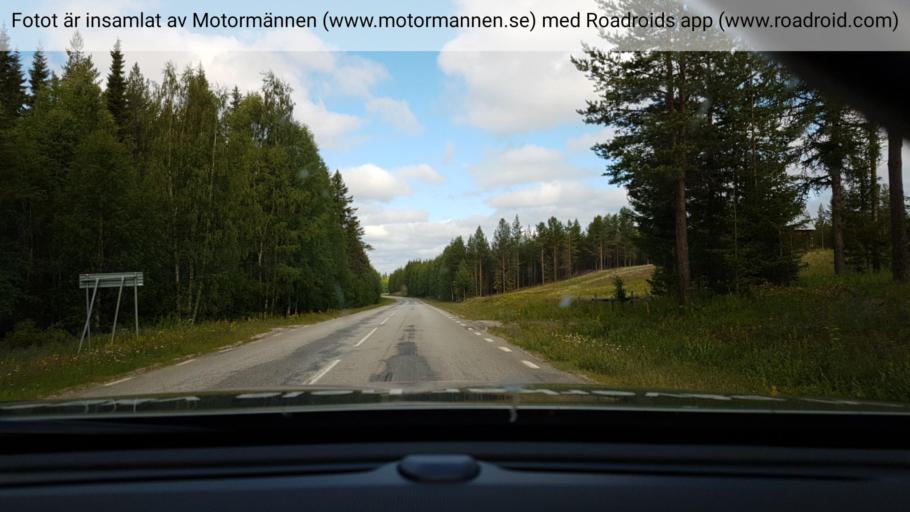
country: SE
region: Vaesterbotten
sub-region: Lycksele Kommun
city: Lycksele
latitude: 64.7714
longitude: 19.0279
